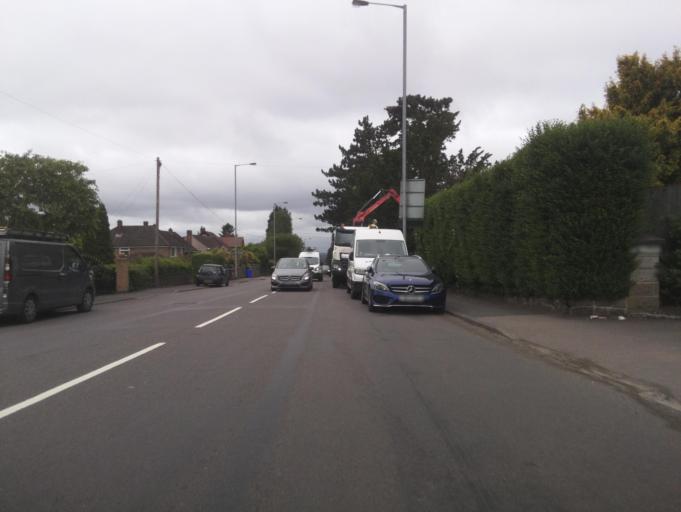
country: GB
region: England
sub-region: Staffordshire
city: Burton upon Trent
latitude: 52.8023
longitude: -1.5976
